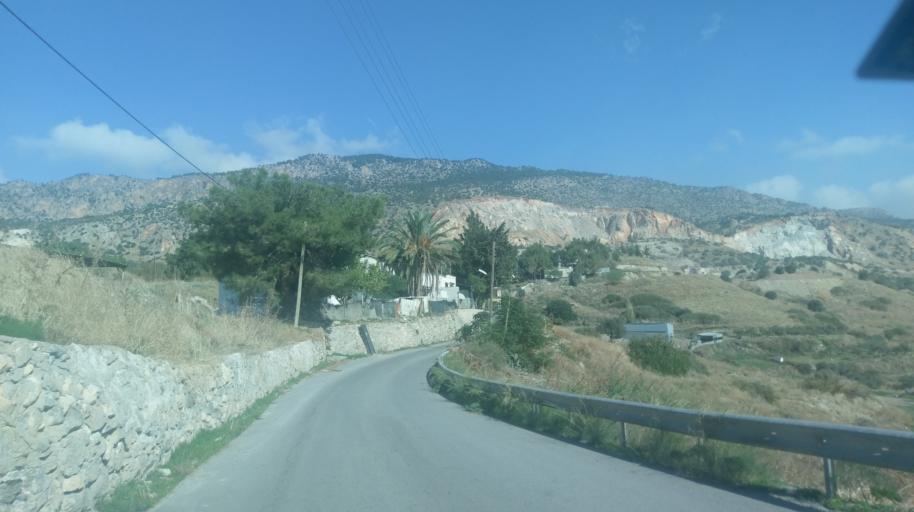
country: CY
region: Lefkosia
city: Nicosia
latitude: 35.2638
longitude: 33.4210
